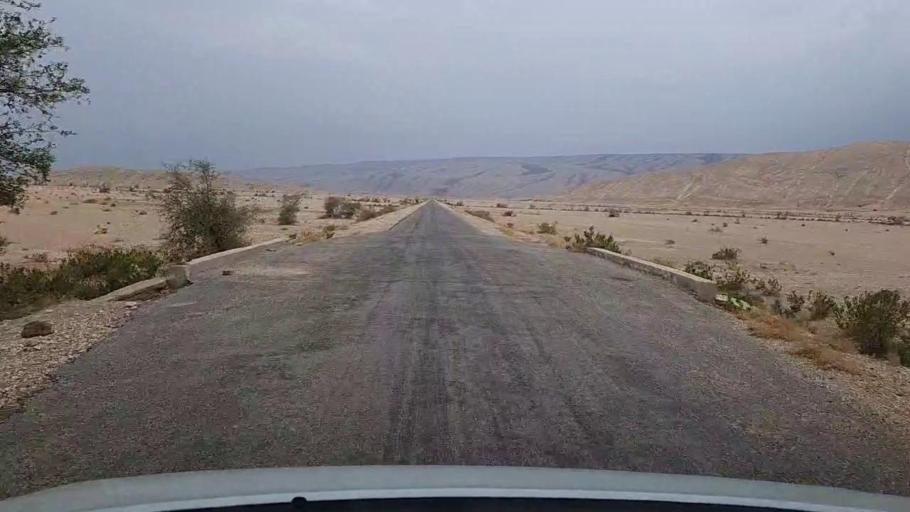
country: PK
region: Sindh
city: Sehwan
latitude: 26.2396
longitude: 67.7126
